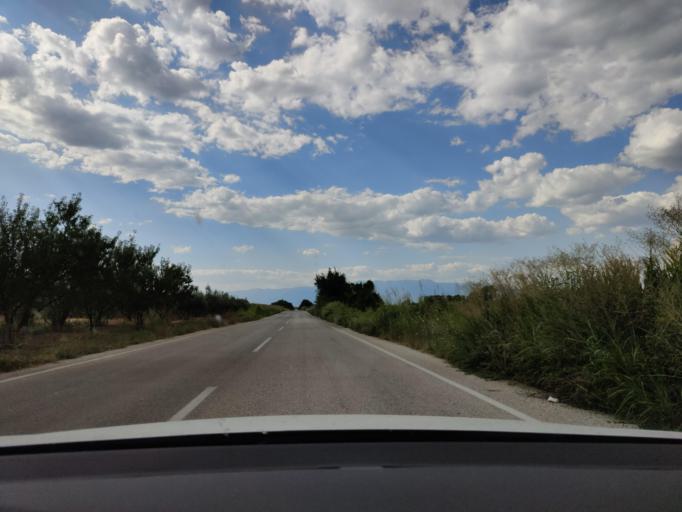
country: GR
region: Central Macedonia
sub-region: Nomos Serron
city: Strymoniko
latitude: 41.0651
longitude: 23.3069
